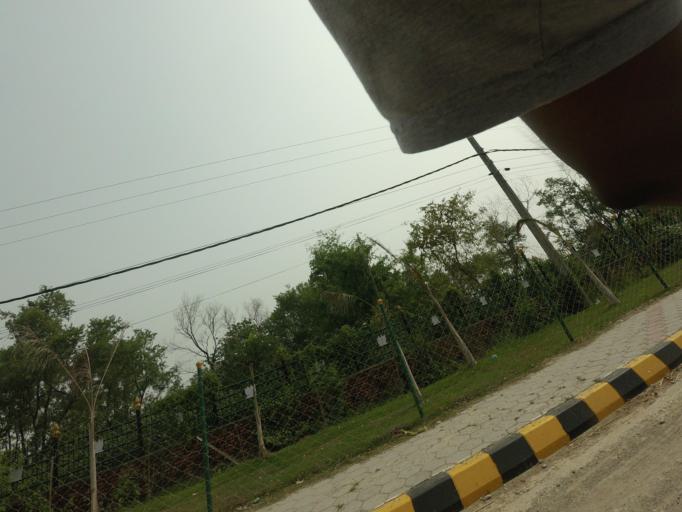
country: IN
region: Uttar Pradesh
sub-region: Maharajganj
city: Nautanwa
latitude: 27.4916
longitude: 83.2696
